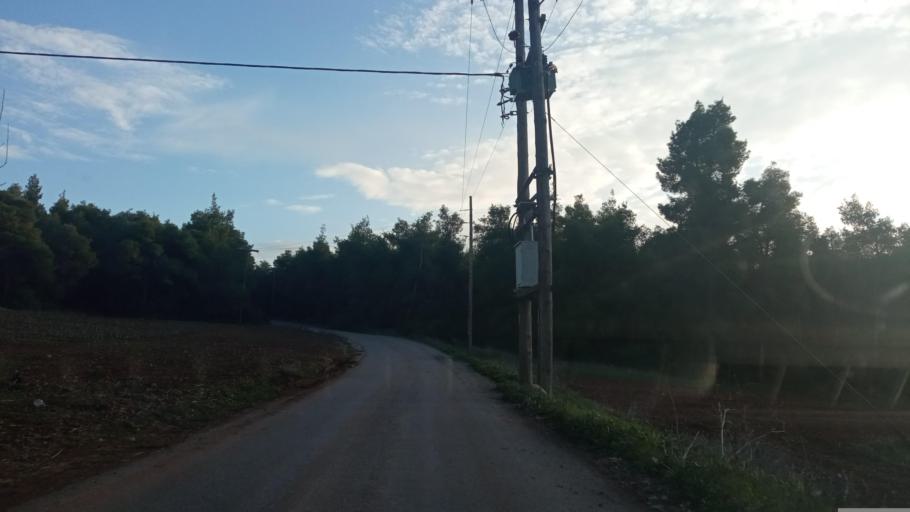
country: GR
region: Central Greece
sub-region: Nomos Evvoias
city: Kastella
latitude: 38.5638
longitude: 23.7096
